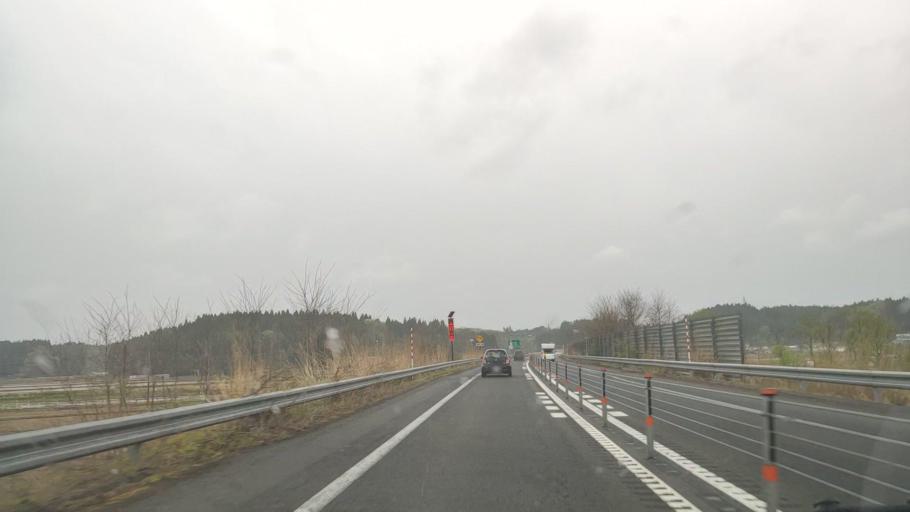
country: JP
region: Akita
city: Noshiromachi
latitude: 40.1869
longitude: 140.0986
